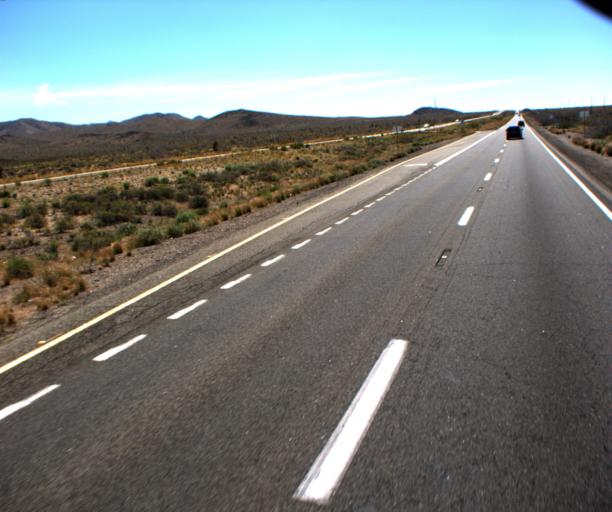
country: US
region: Arizona
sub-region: Mohave County
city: Dolan Springs
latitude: 35.4571
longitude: -114.3025
